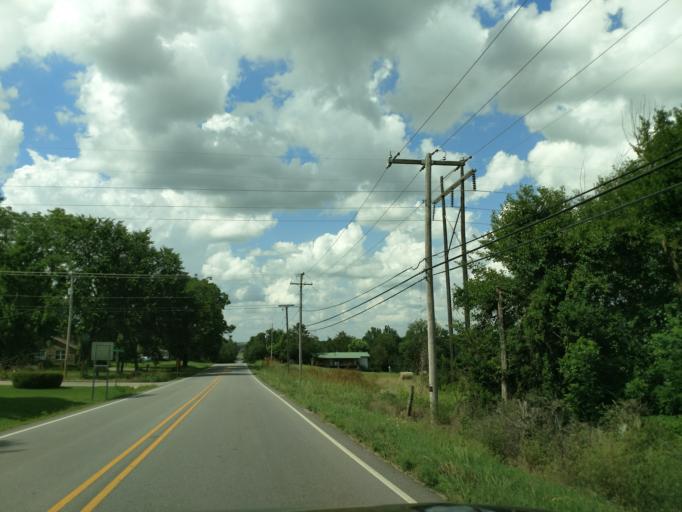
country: US
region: Arkansas
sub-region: Carroll County
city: Berryville
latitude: 36.3772
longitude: -93.5673
